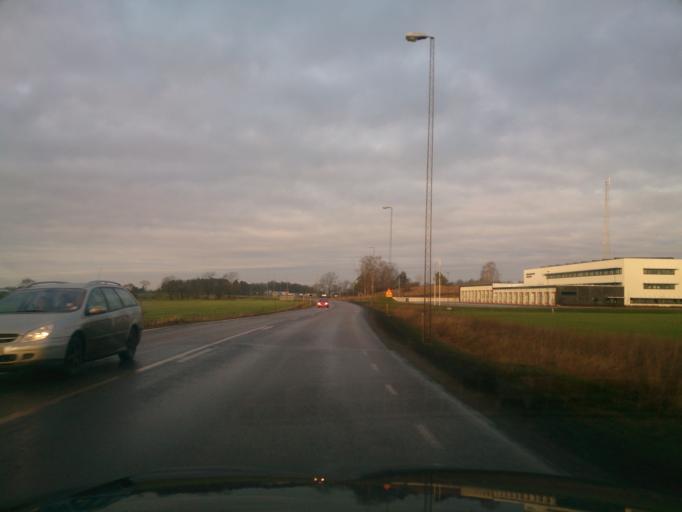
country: SE
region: OEstergoetland
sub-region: Linkopings Kommun
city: Linkoping
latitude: 58.4191
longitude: 15.6549
